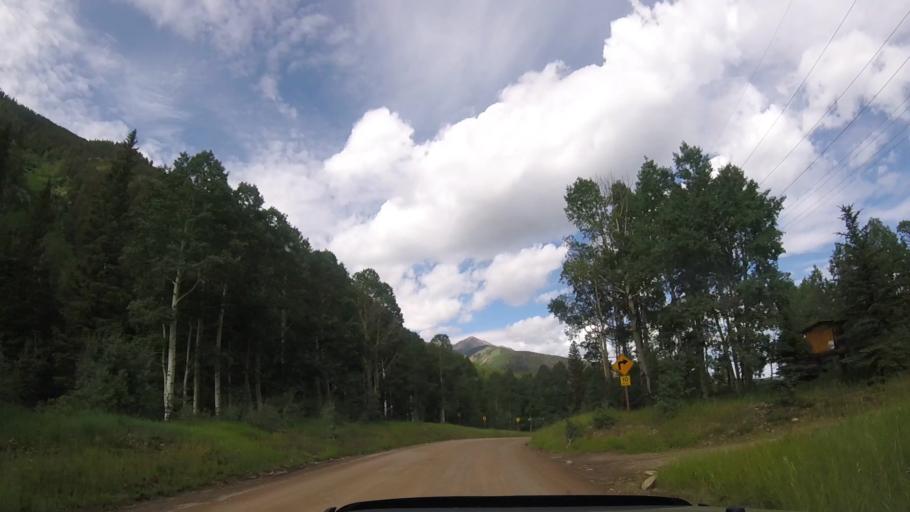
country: US
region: Colorado
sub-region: San Miguel County
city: Mountain Village
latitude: 37.8591
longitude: -107.8674
